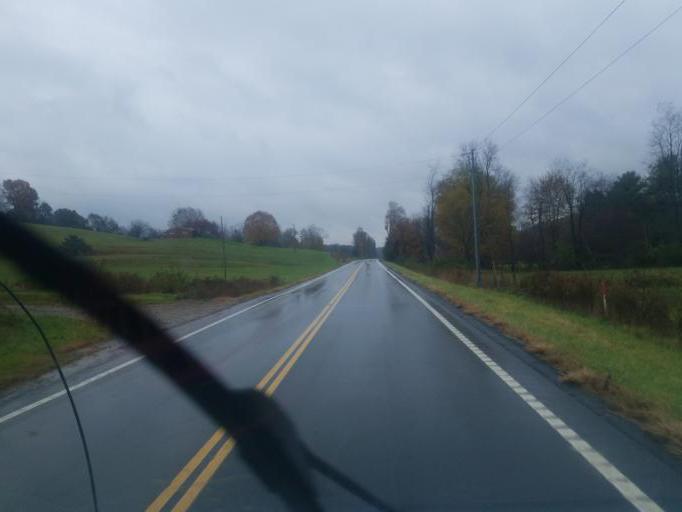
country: US
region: Ohio
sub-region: Muskingum County
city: Frazeysburg
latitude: 40.1751
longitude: -82.2278
